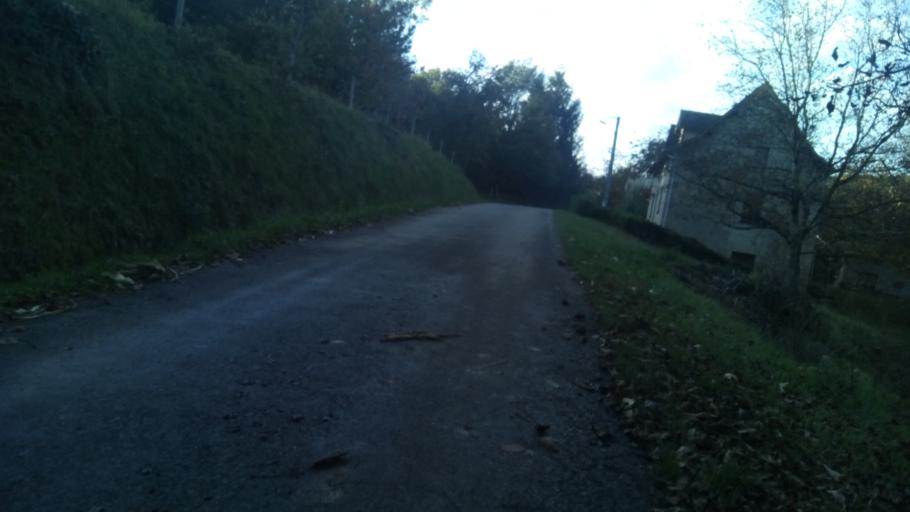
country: FR
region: Midi-Pyrenees
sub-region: Departement du Lot
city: Cajarc
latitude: 44.4726
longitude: 1.8292
